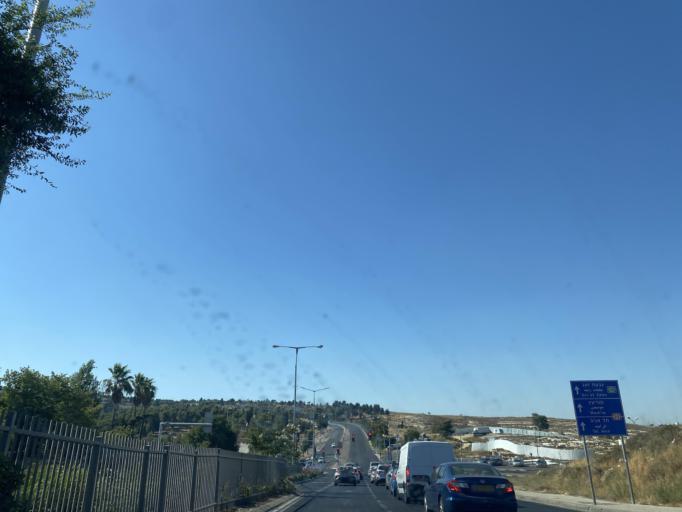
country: PS
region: West Bank
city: Bayt Iksa
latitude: 31.8248
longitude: 35.1889
